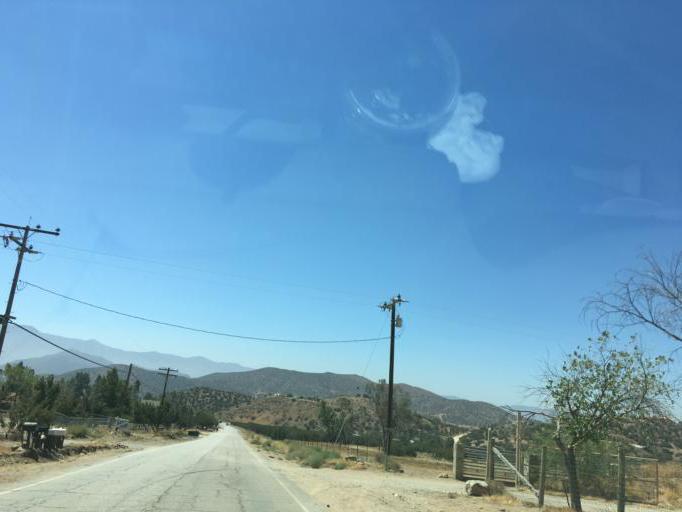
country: US
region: California
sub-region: Los Angeles County
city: Acton
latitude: 34.5212
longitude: -118.2380
